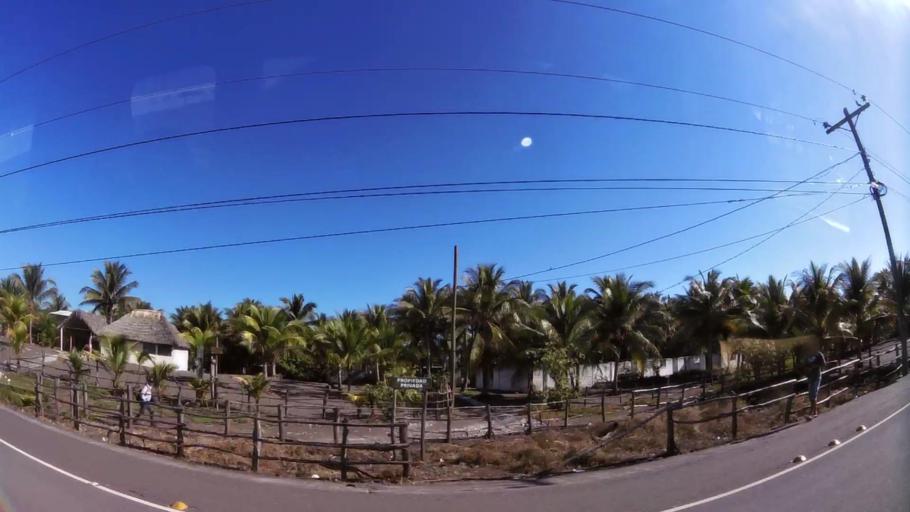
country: GT
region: Santa Rosa
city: Guazacapan
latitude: 13.8625
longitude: -90.4040
